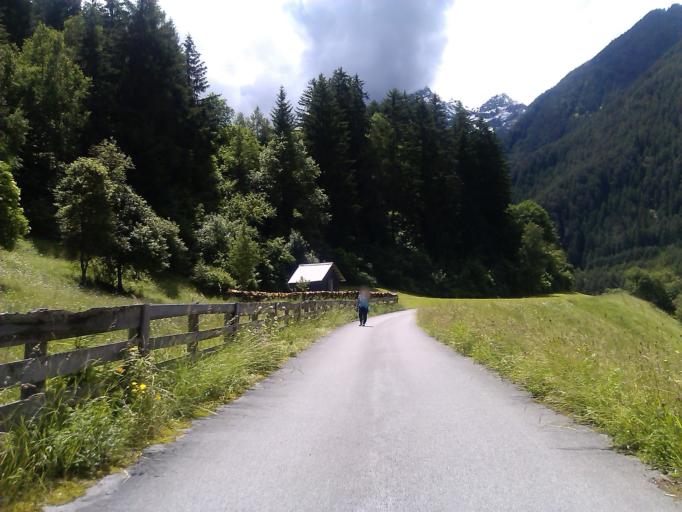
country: AT
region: Tyrol
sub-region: Politischer Bezirk Landeck
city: Pfunds
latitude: 46.9558
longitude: 10.5196
